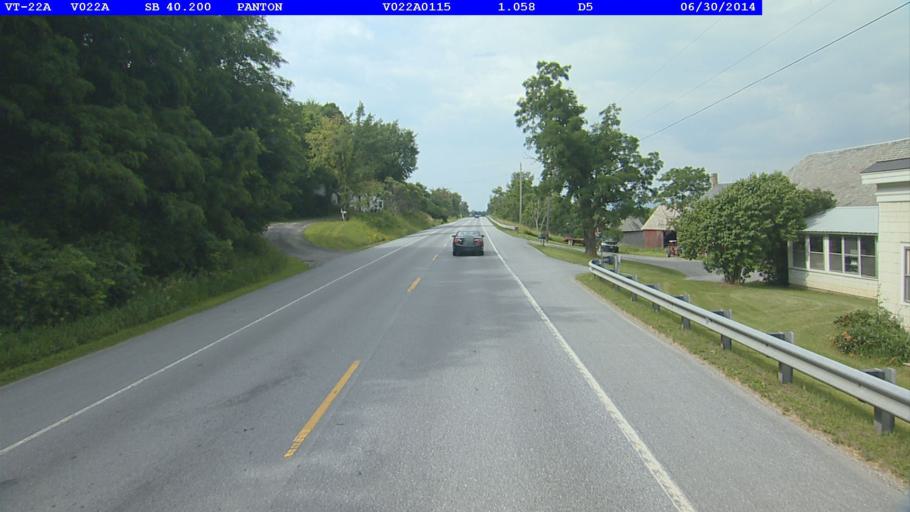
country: US
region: Vermont
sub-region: Addison County
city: Vergennes
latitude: 44.1335
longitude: -73.2852
